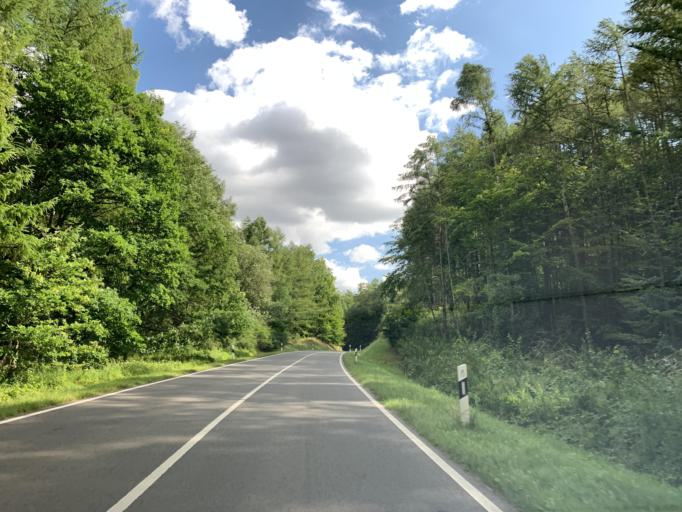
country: DE
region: Mecklenburg-Vorpommern
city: Wustrow
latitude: 53.4184
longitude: 13.1773
